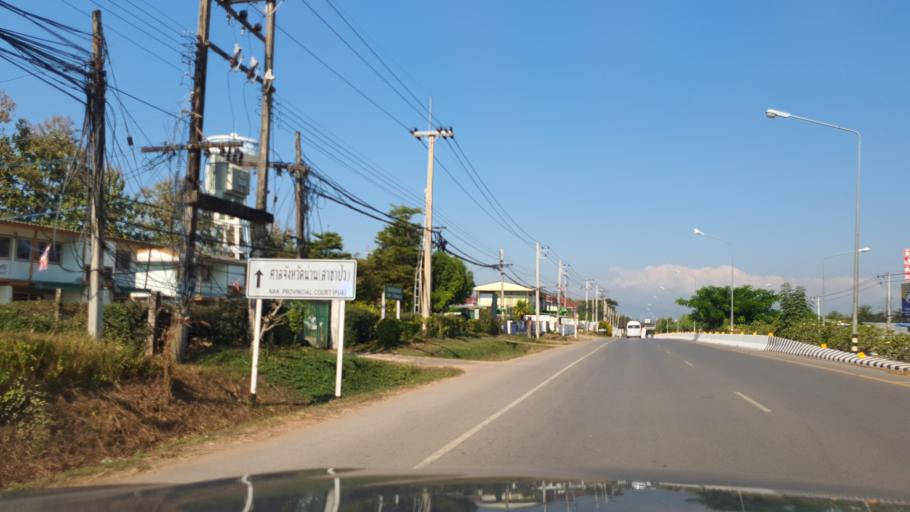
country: TH
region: Nan
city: Pua
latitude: 19.1729
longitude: 100.9187
